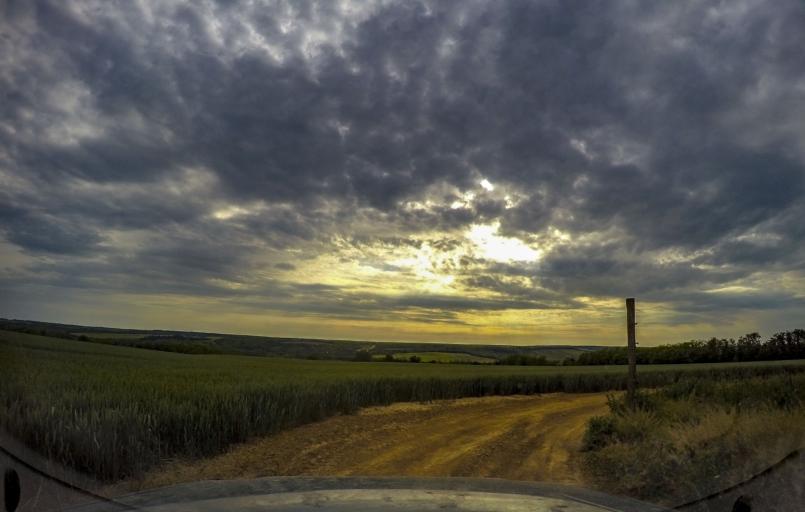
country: HU
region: Somogy
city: Karad
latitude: 46.6650
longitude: 17.7986
